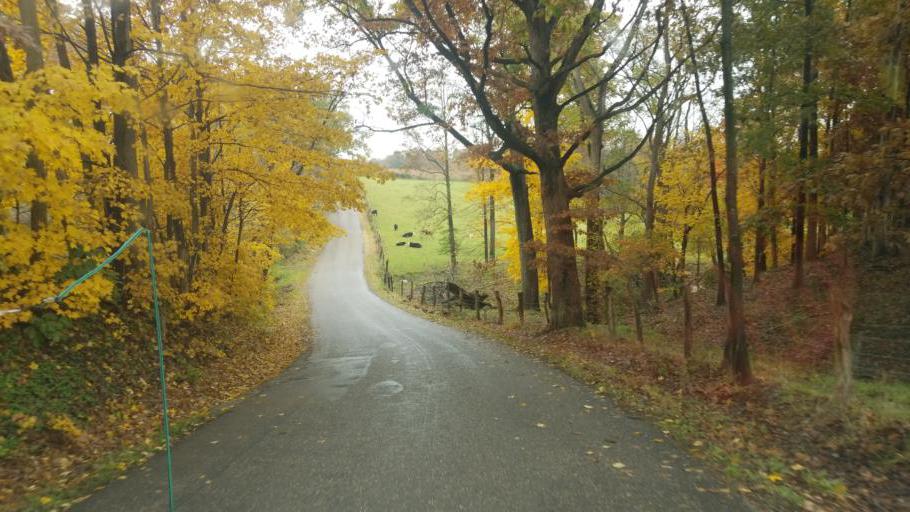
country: US
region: Ohio
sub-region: Washington County
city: Beverly
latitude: 39.5428
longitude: -81.7053
